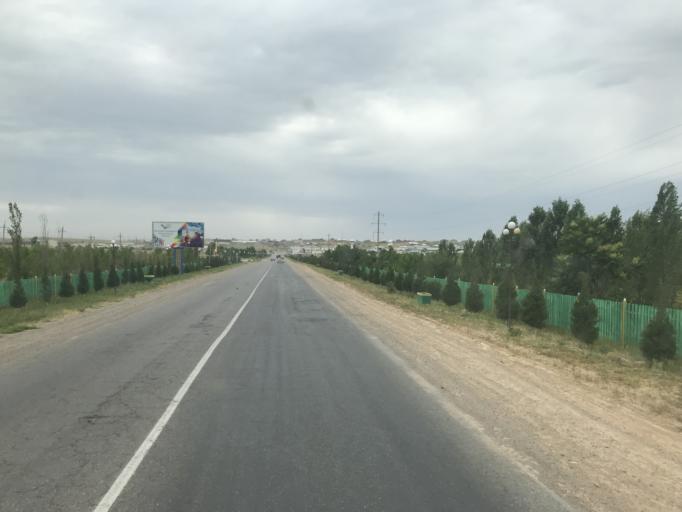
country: KZ
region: Ongtustik Qazaqstan
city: Saryaghash
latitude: 41.4766
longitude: 69.2196
